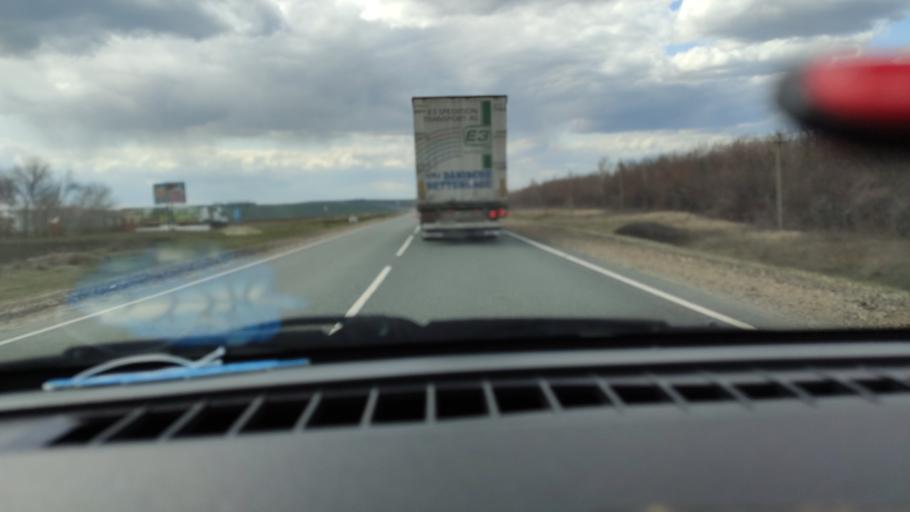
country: RU
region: Saratov
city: Alekseyevka
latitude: 52.2623
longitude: 47.9220
